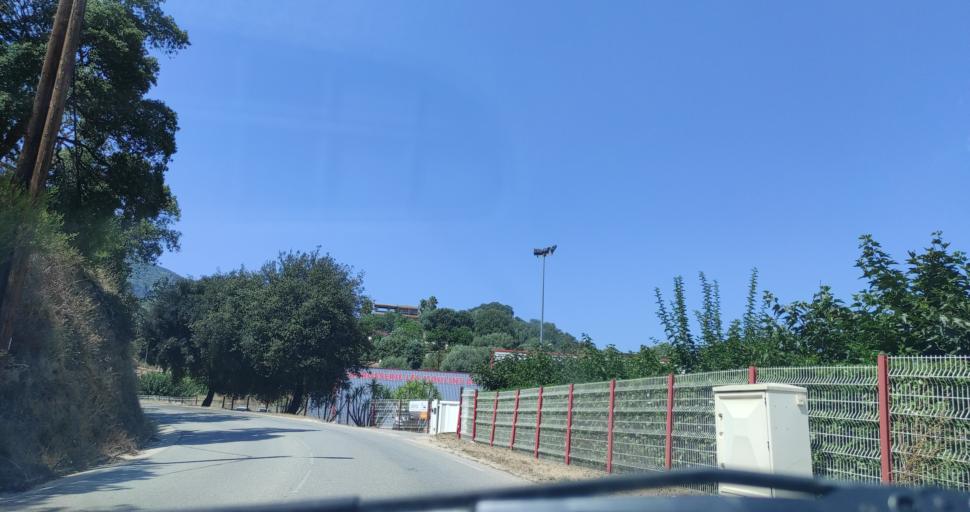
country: FR
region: Corsica
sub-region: Departement de la Corse-du-Sud
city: Ajaccio
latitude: 41.9421
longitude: 8.7355
